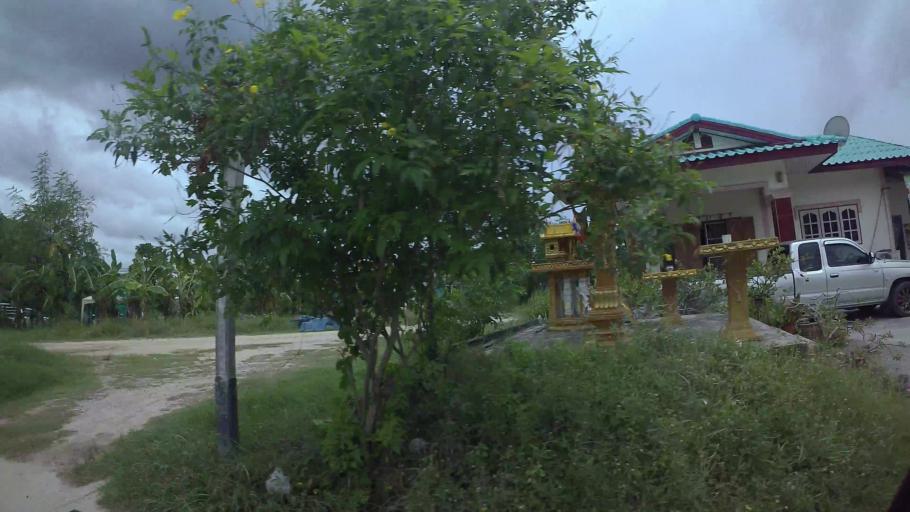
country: TH
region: Chon Buri
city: Si Racha
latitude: 13.1615
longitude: 100.9717
